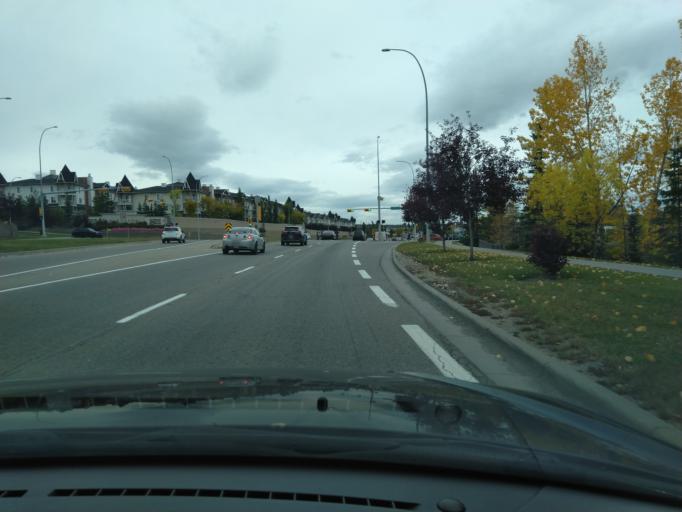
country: CA
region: Alberta
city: Calgary
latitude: 51.1559
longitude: -114.0693
